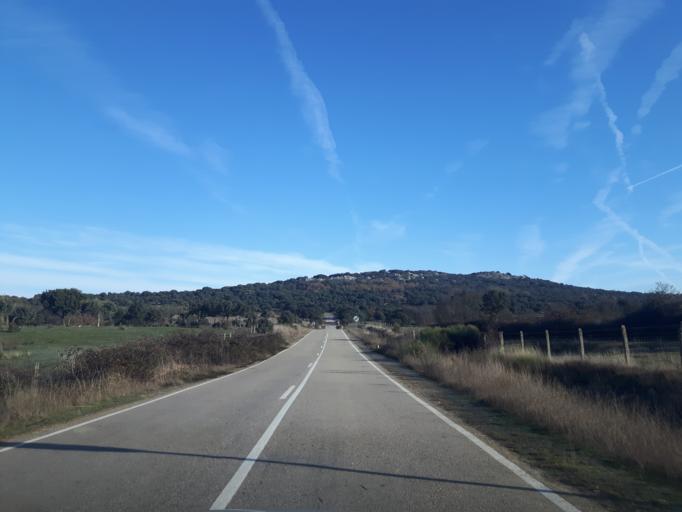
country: ES
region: Castille and Leon
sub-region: Provincia de Salamanca
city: Olmedo de Camaces
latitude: 40.8907
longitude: -6.6226
